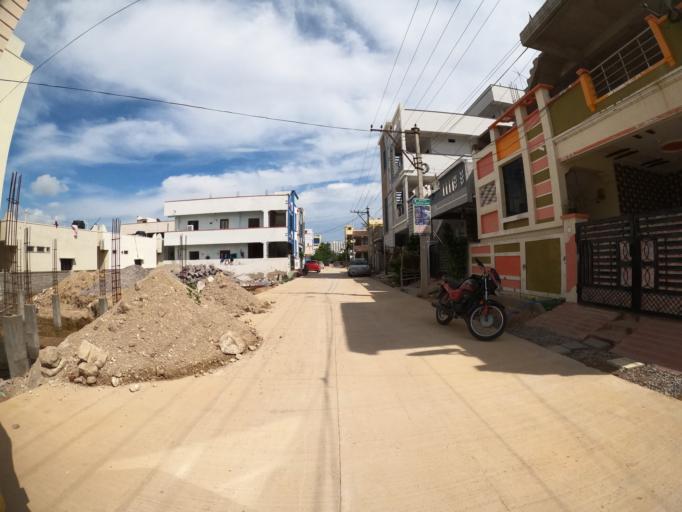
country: IN
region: Telangana
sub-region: Hyderabad
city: Hyderabad
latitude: 17.3624
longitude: 78.3810
